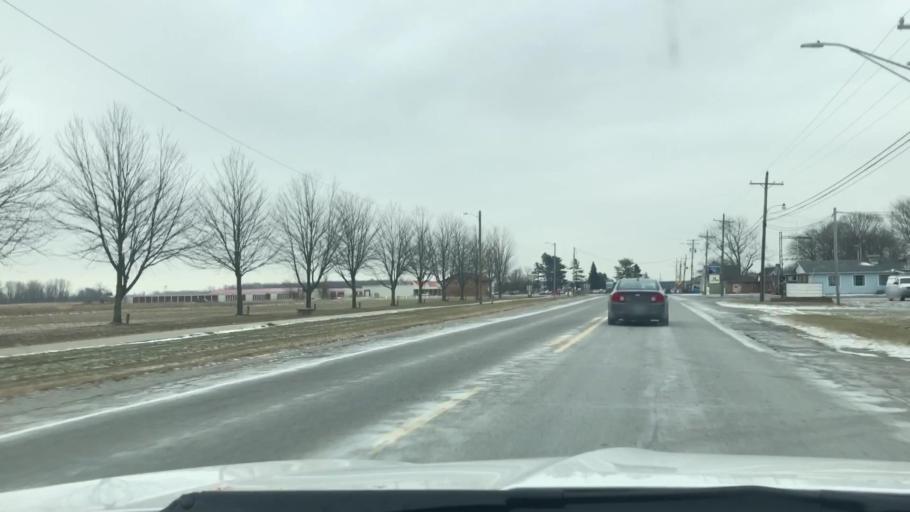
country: US
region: Indiana
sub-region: Fulton County
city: Rochester
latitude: 41.0618
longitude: -86.1867
